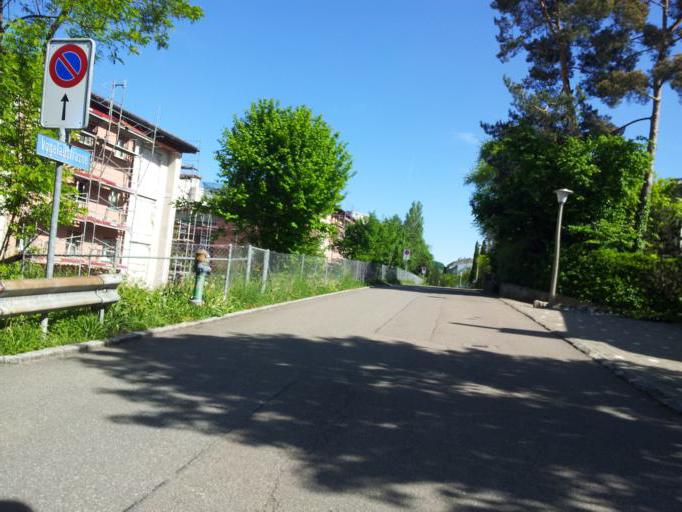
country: CH
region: Zurich
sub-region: Bezirk Dietikon
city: Dietikon / Hofacker
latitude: 47.3964
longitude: 8.4127
